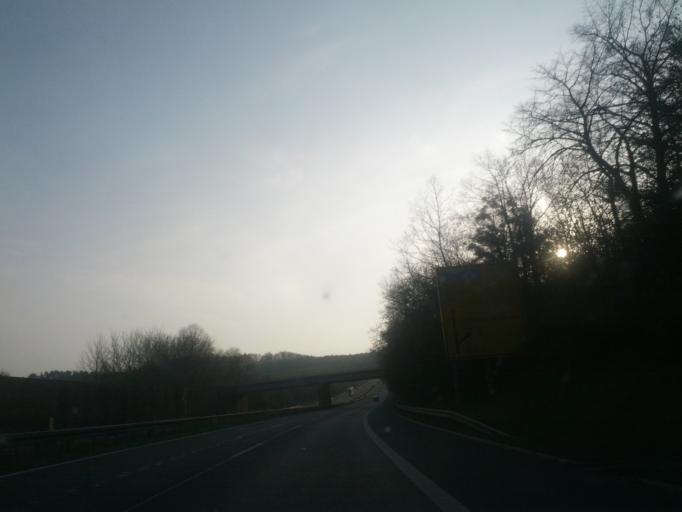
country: DE
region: Thuringia
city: Eisenach
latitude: 50.9967
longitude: 10.3002
